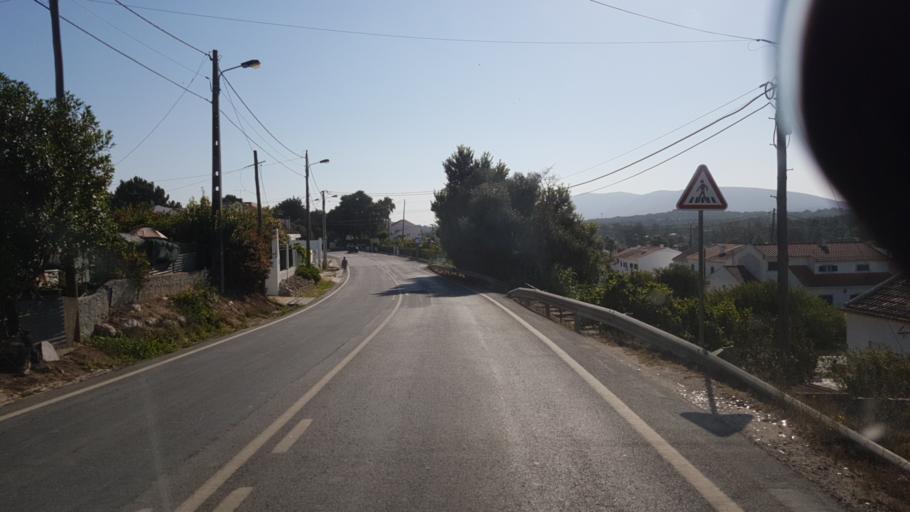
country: PT
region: Setubal
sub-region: Sesimbra
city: Sesimbra
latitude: 38.4687
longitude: -9.0905
